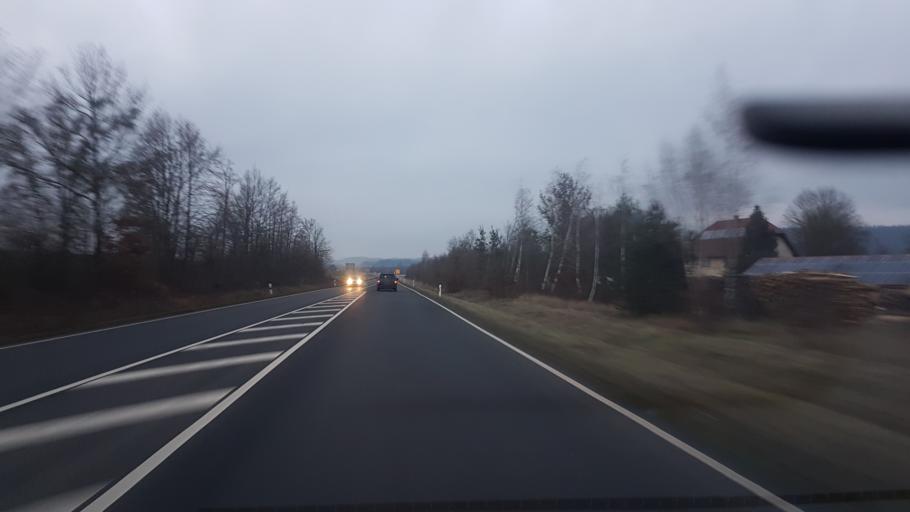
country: DE
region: Bavaria
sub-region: Regierungsbezirk Unterfranken
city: Pfarrweisach
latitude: 50.1263
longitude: 10.7607
